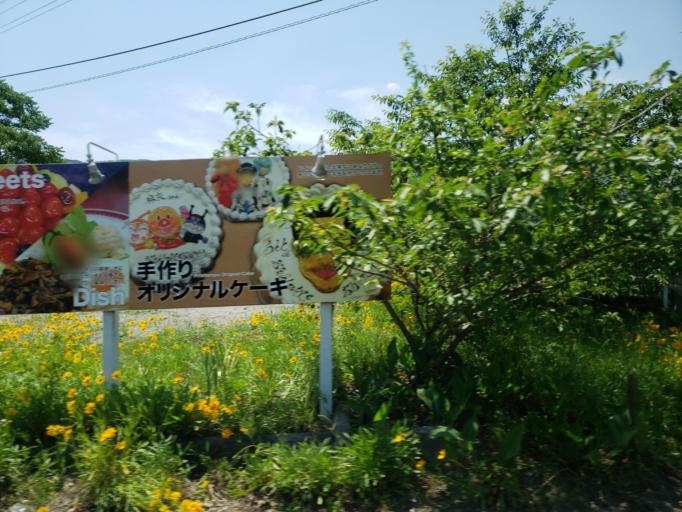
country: JP
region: Tokushima
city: Wakimachi
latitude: 34.0659
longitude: 134.1778
